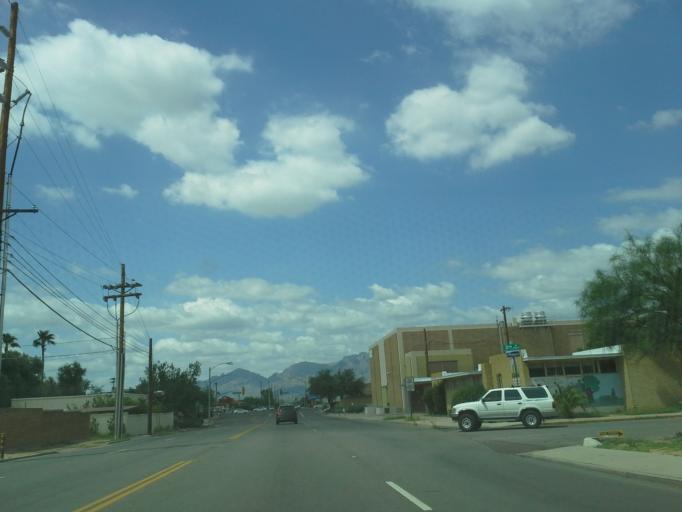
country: US
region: Arizona
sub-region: Pima County
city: Tucson
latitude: 32.2339
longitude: -110.9267
